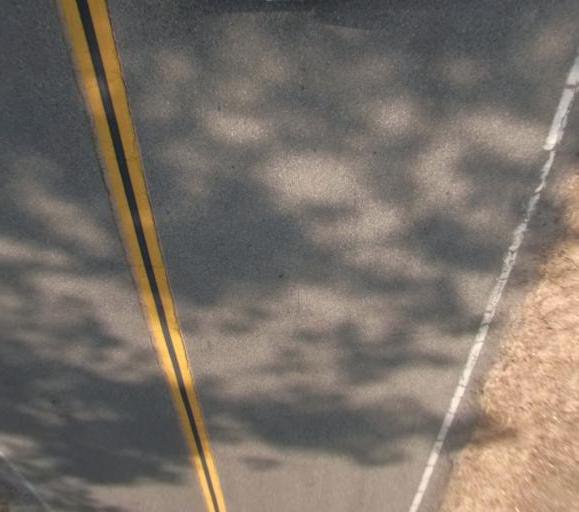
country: US
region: California
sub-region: Madera County
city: Oakhurst
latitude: 37.2335
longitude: -119.5276
